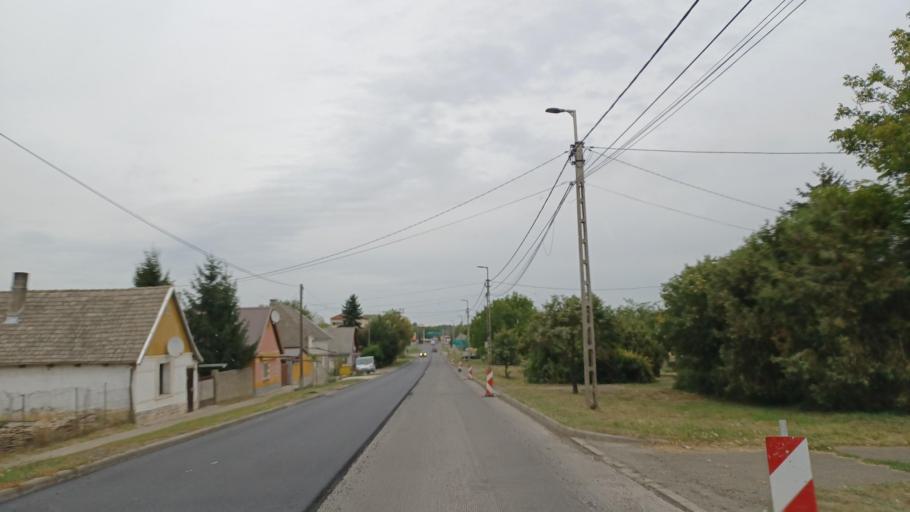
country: HU
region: Tolna
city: Dunafoldvar
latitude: 46.8127
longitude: 18.9035
